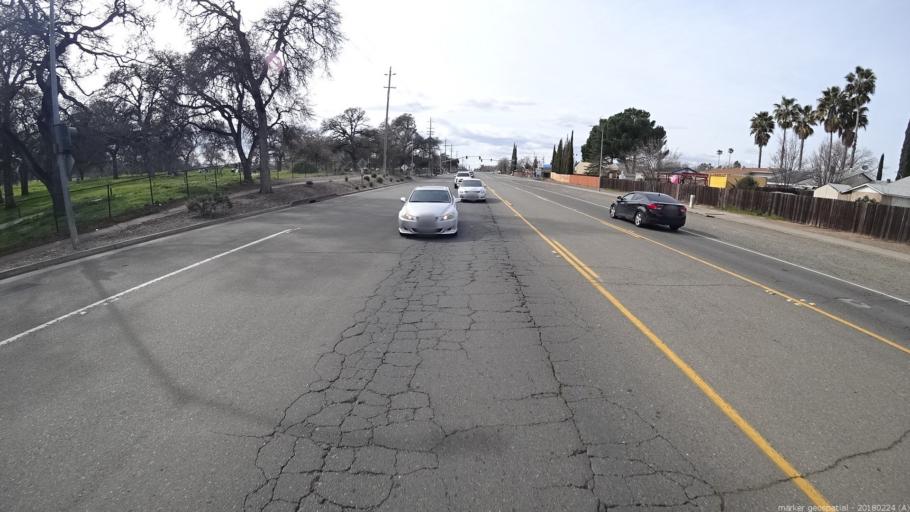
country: US
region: California
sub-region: Sacramento County
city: North Highlands
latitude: 38.7143
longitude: -121.4062
